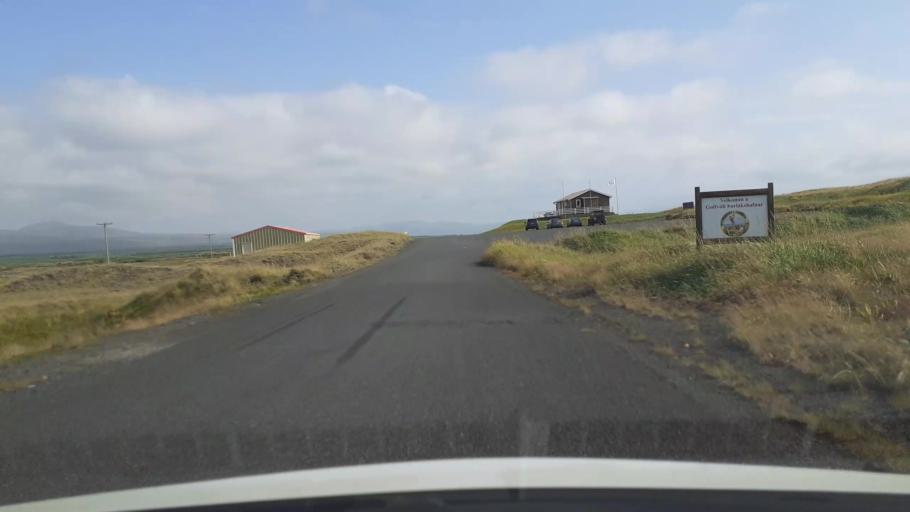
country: IS
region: South
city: THorlakshoefn
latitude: 63.8691
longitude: -21.3754
